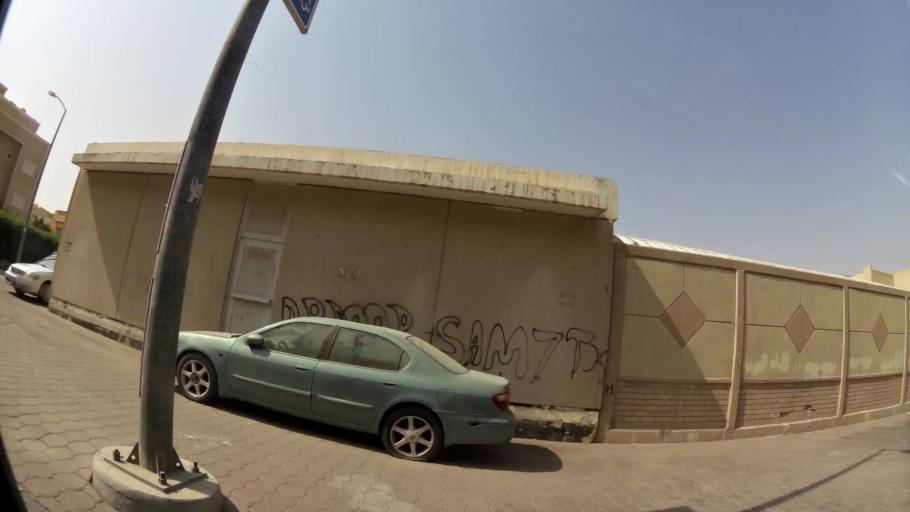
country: KW
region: Muhafazat al Jahra'
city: Al Jahra'
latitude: 29.3049
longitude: 47.7140
